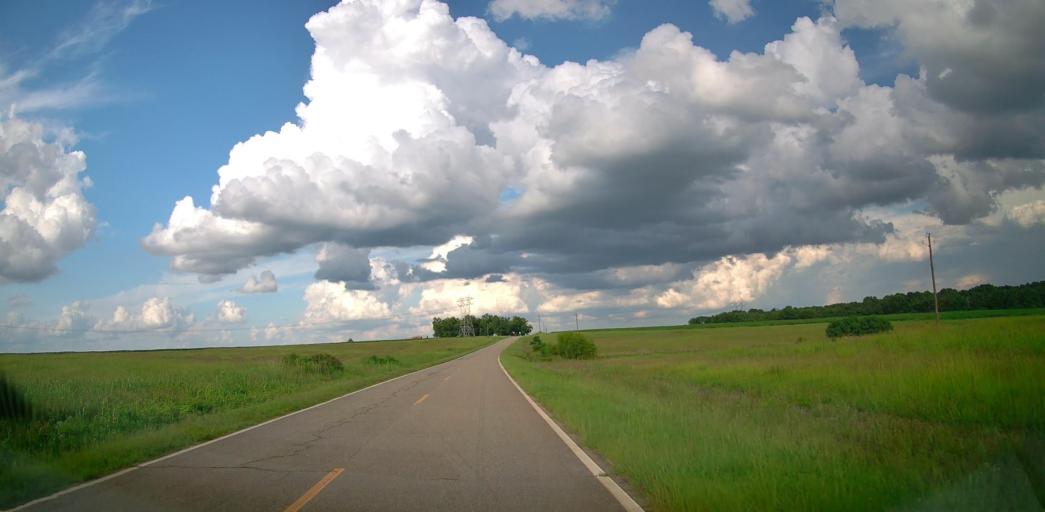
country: US
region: Georgia
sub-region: Bleckley County
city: Cochran
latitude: 32.4058
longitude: -83.4157
